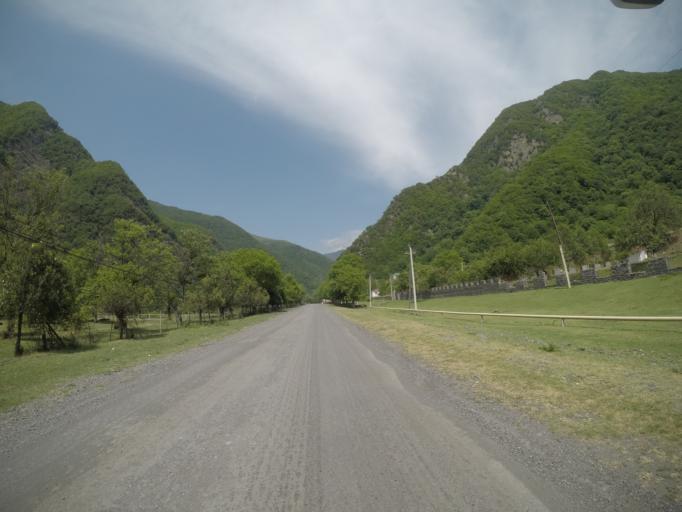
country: AZ
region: Qakh Rayon
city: Qaxbas
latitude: 41.4601
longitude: 47.0282
